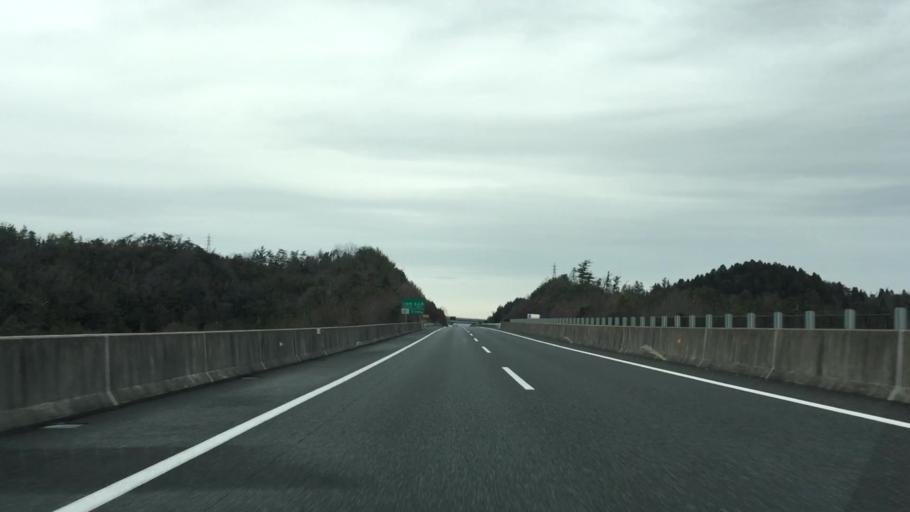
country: JP
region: Gifu
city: Toki
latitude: 35.3231
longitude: 137.1761
